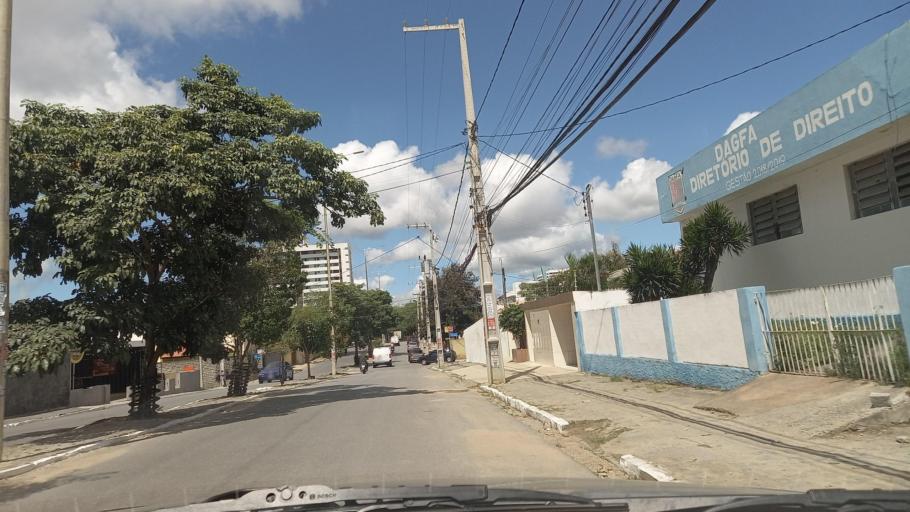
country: BR
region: Pernambuco
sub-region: Caruaru
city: Caruaru
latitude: -8.2659
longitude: -35.9644
